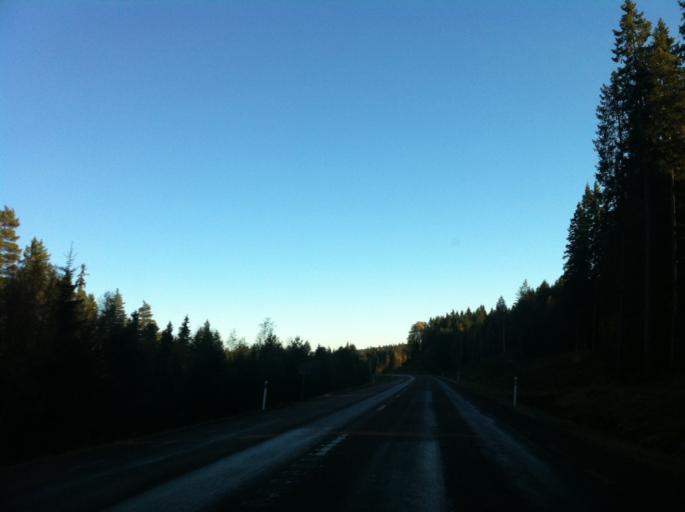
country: SE
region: Dalarna
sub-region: Faluns Kommun
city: Bjursas
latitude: 60.7548
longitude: 15.3423
